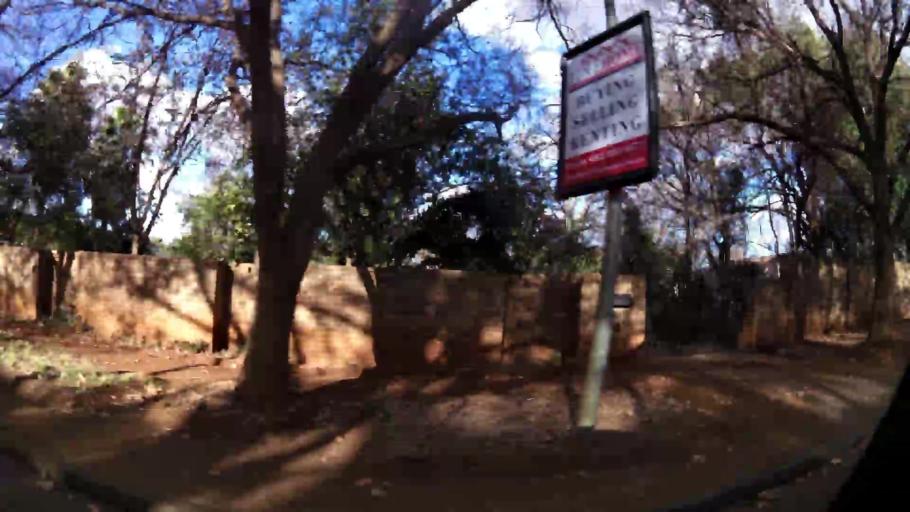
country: ZA
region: North-West
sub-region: Dr Kenneth Kaunda District Municipality
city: Potchefstroom
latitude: -26.6872
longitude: 27.0994
